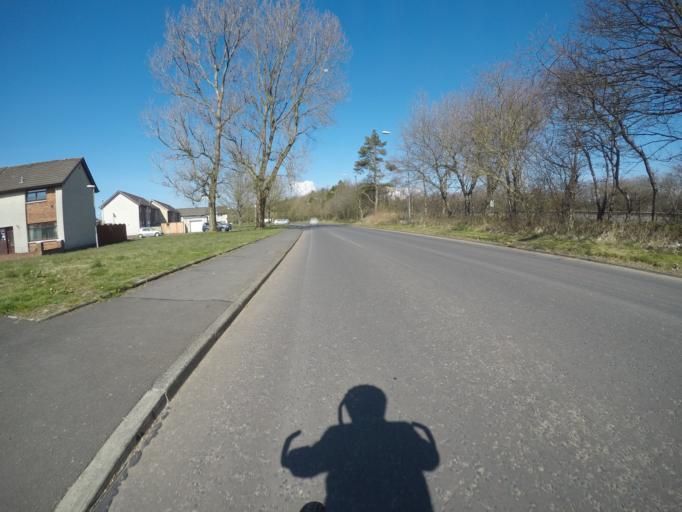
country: GB
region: Scotland
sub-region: North Ayrshire
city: Irvine
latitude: 55.6342
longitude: -4.6601
